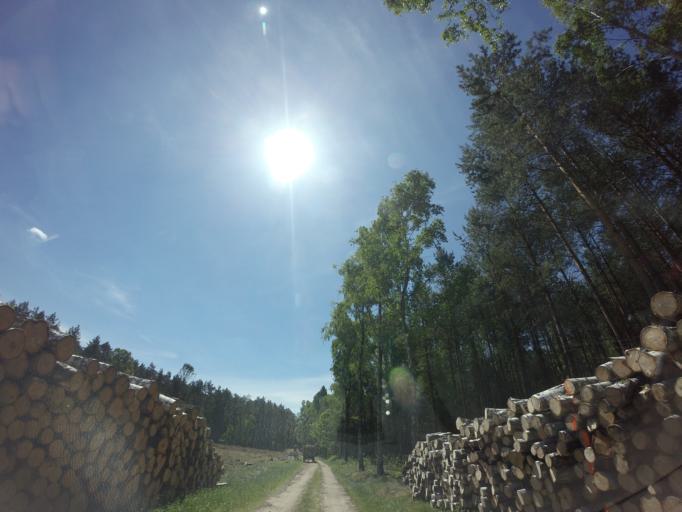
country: PL
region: West Pomeranian Voivodeship
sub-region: Powiat choszczenski
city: Drawno
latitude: 53.2591
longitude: 15.7466
